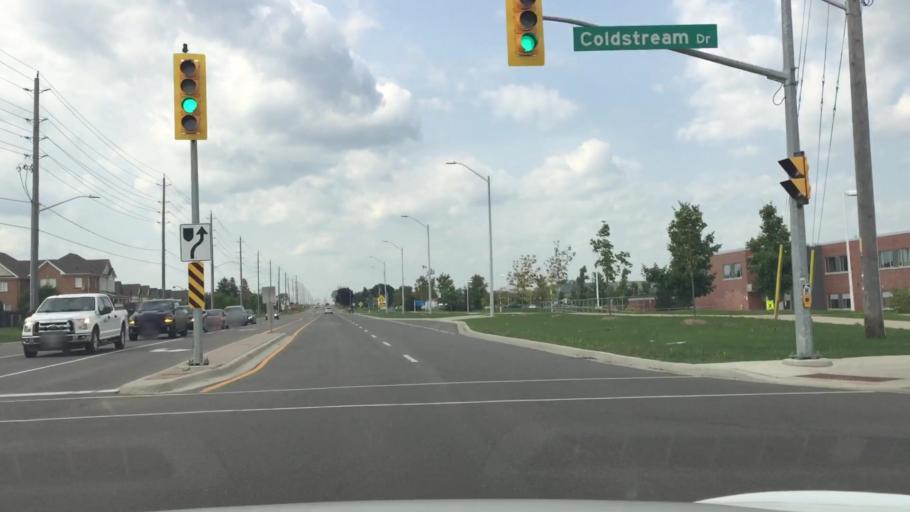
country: CA
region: Ontario
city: Oshawa
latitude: 43.9447
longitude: -78.8516
